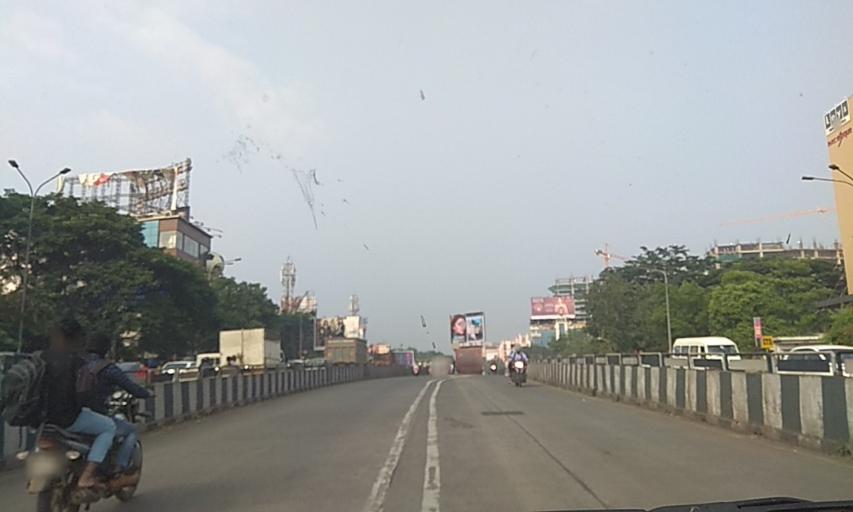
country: IN
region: Maharashtra
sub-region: Pune Division
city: Lohogaon
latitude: 18.5615
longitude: 73.9206
